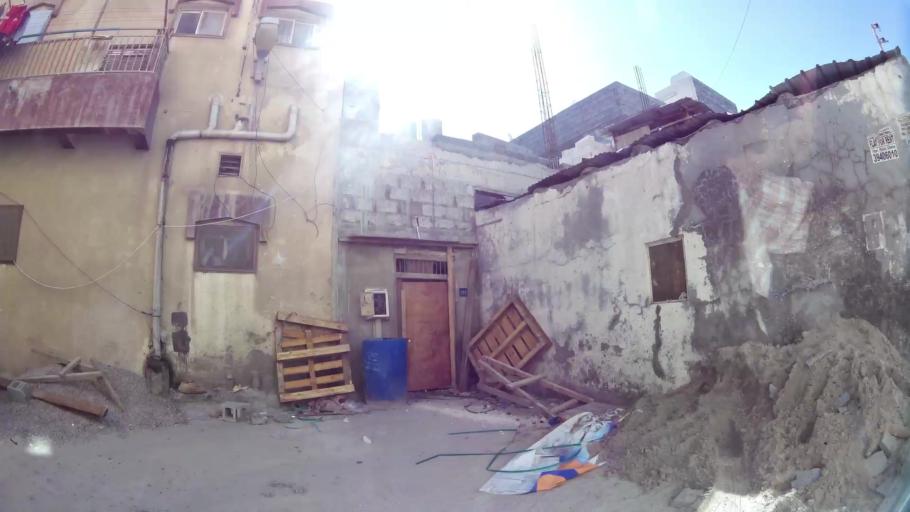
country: BH
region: Muharraq
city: Al Muharraq
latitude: 26.2577
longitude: 50.6116
